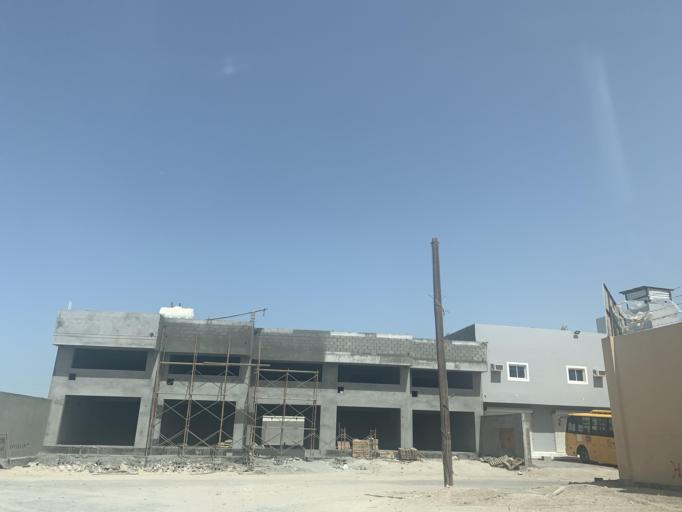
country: BH
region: Northern
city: Sitrah
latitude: 26.1762
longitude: 50.6129
